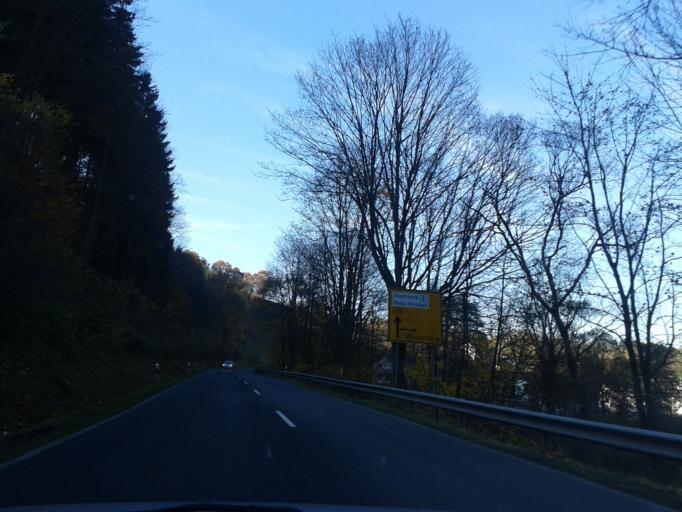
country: DE
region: North Rhine-Westphalia
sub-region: Regierungsbezirk Arnsberg
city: Bad Berleburg
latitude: 51.0352
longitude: 8.3864
